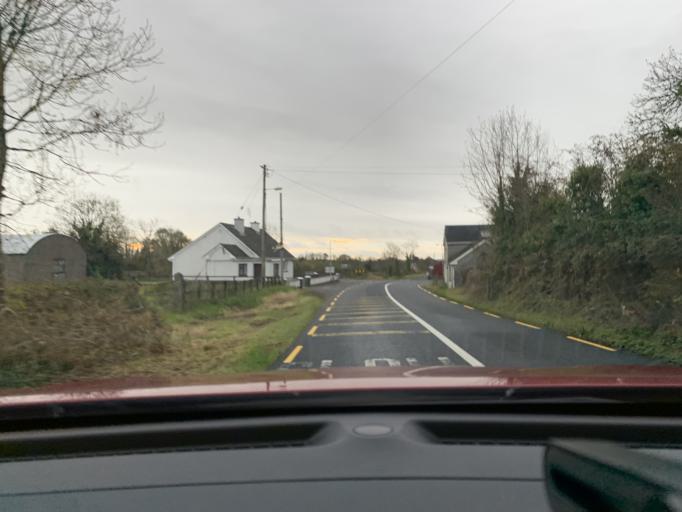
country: IE
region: Connaught
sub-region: Roscommon
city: Ballaghaderreen
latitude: 53.9287
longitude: -8.5295
